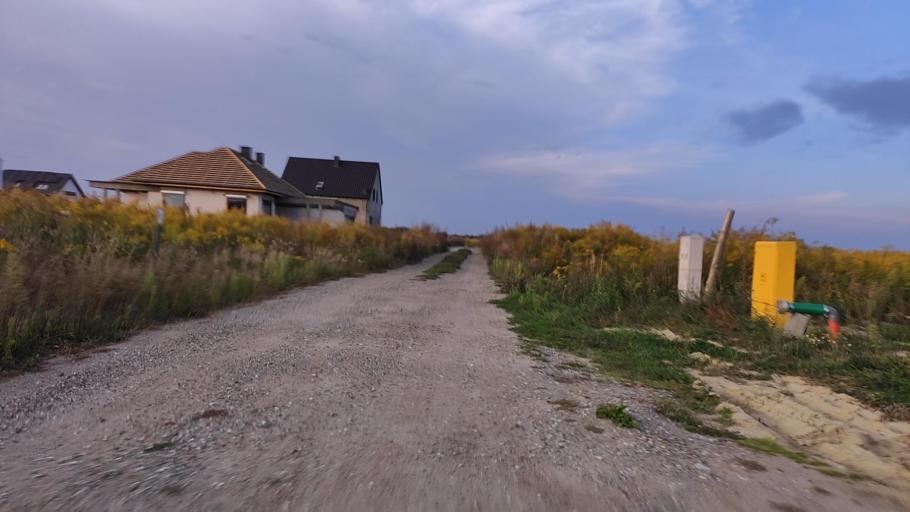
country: PL
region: Greater Poland Voivodeship
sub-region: Powiat poznanski
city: Kleszczewo
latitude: 52.3900
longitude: 17.1694
